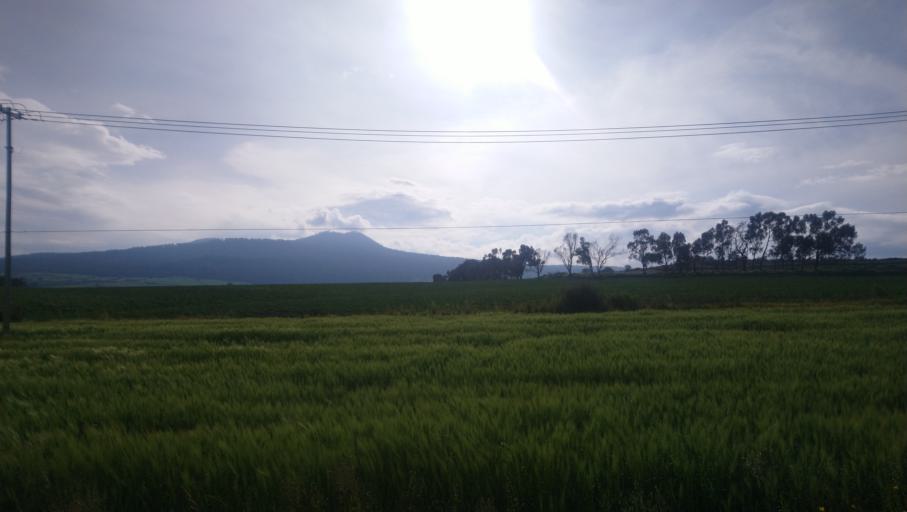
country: MX
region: Mexico
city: Juchitepec de Mariano Riva Palacio
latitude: 19.1182
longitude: -98.9364
